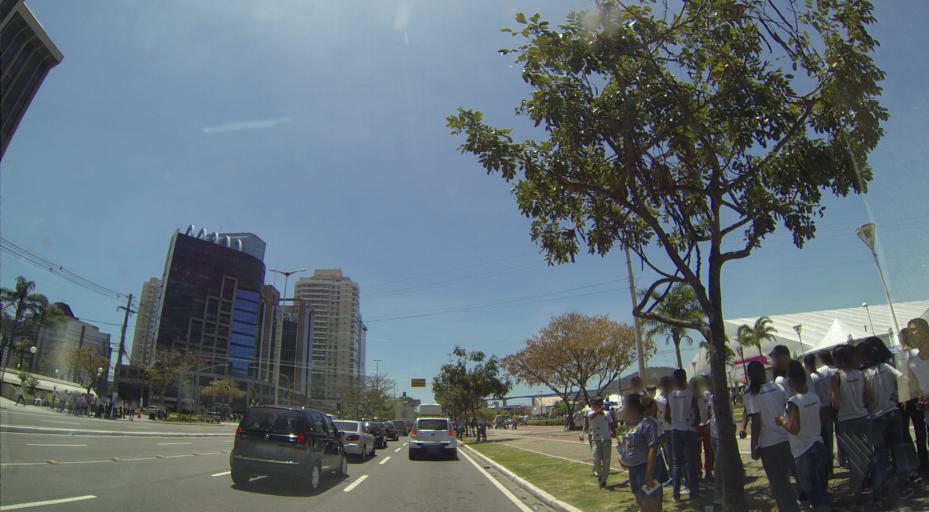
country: BR
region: Espirito Santo
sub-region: Vila Velha
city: Vila Velha
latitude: -20.3162
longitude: -40.2956
